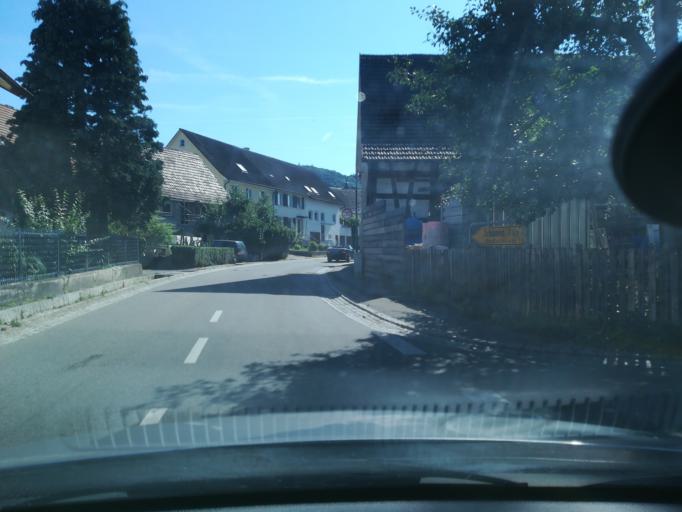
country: DE
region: Baden-Wuerttemberg
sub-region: Freiburg Region
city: Moos
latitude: 47.7185
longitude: 8.8953
